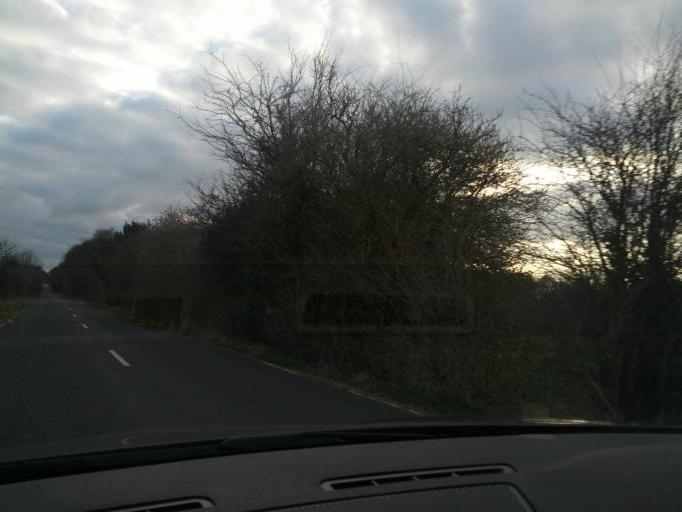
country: IE
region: Leinster
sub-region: Uibh Fhaili
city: Banagher
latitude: 53.2848
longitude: -8.0288
